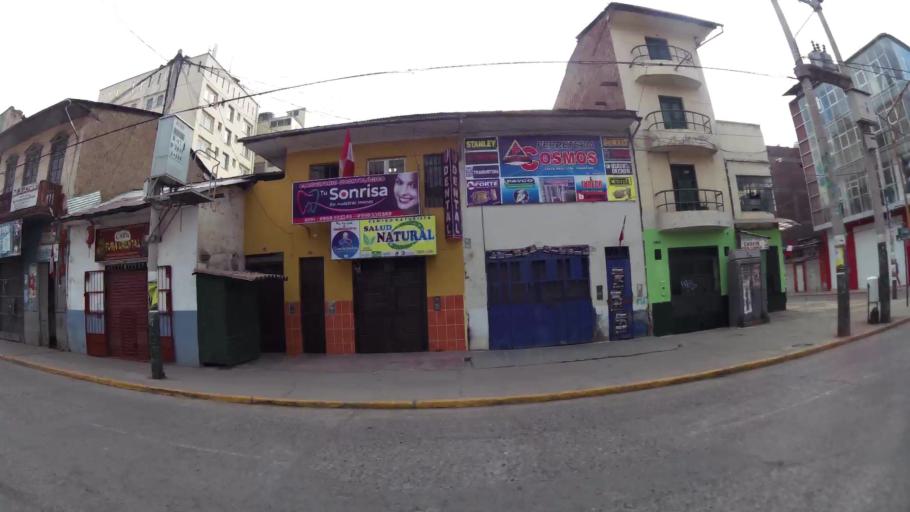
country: PE
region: Junin
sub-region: Provincia de Huancayo
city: Huancayo
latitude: -12.0740
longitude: -75.2069
